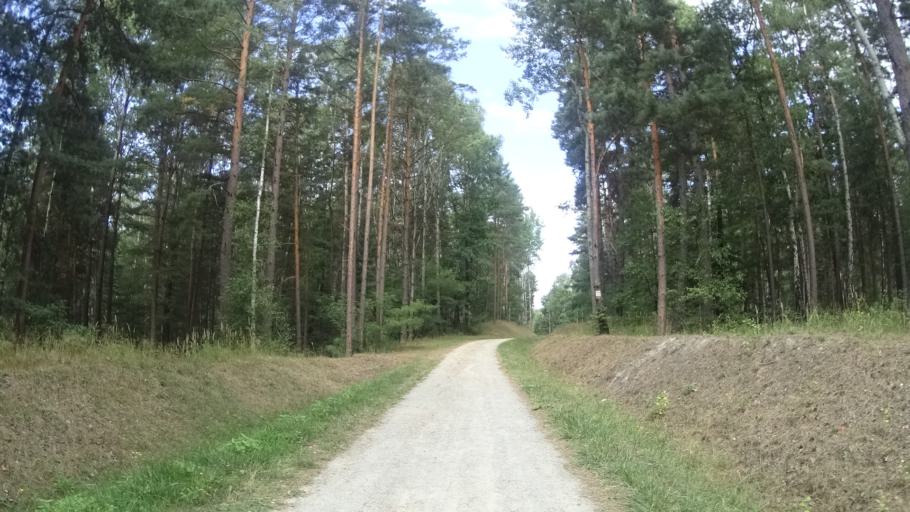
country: PL
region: Lubusz
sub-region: Powiat zarski
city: Leknica
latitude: 51.5332
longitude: 14.7630
